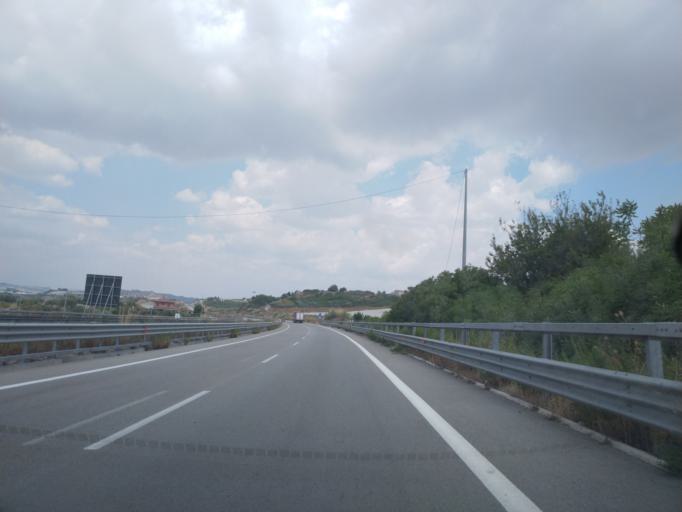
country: IT
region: Sicily
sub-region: Agrigento
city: Canicatti
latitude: 37.3836
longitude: 13.8241
